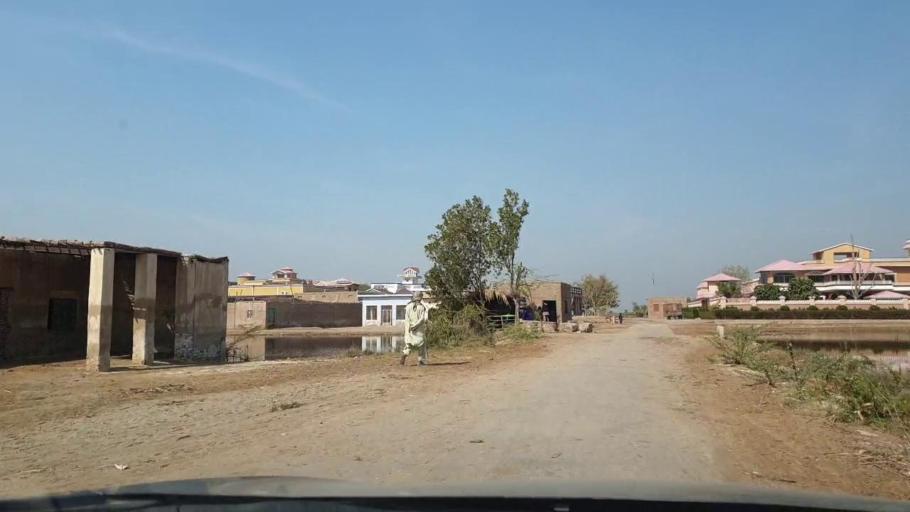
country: PK
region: Sindh
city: Berani
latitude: 25.6889
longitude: 68.7545
